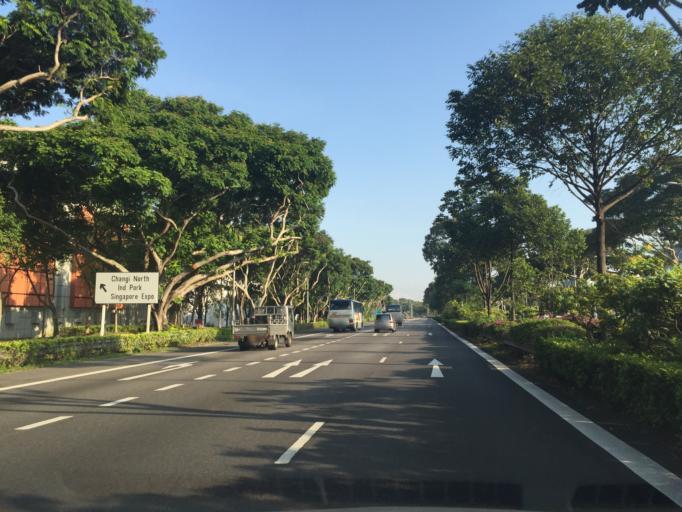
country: SG
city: Singapore
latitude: 1.3442
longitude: 103.9687
